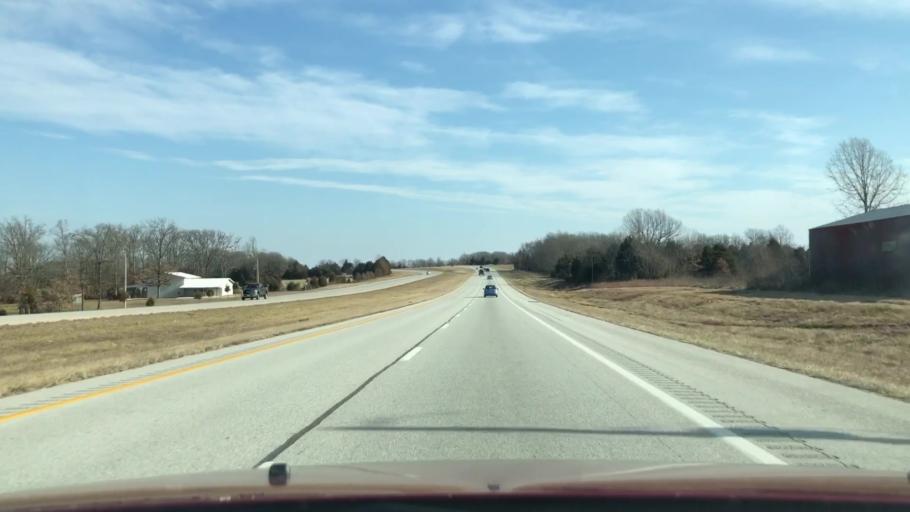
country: US
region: Missouri
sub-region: Webster County
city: Seymour
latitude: 37.1639
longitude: -92.8802
